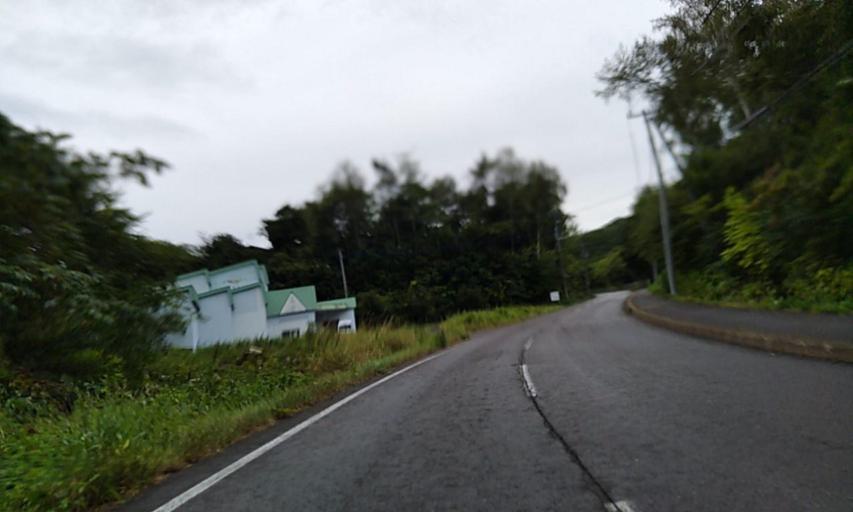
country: JP
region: Hokkaido
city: Abashiri
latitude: 44.0023
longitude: 144.2311
